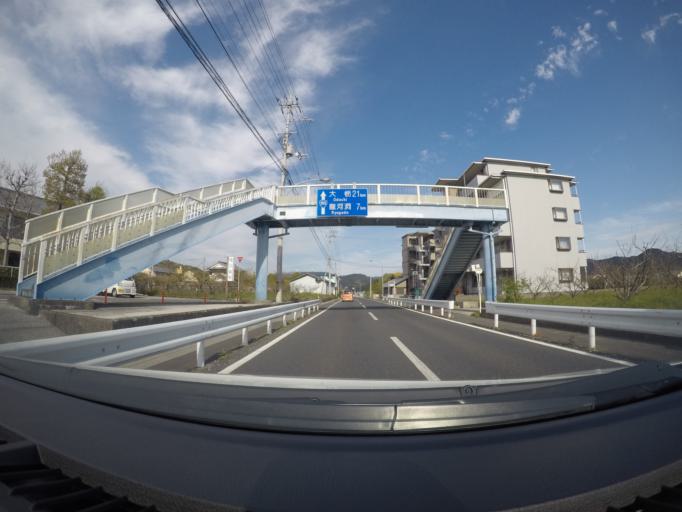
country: JP
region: Kochi
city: Kochi-shi
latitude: 33.6087
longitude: 133.7003
